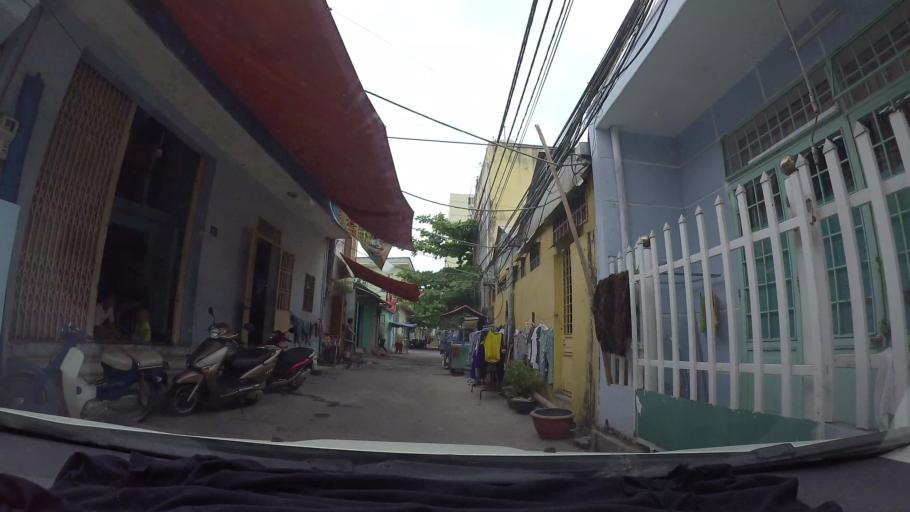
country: VN
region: Da Nang
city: Thanh Khe
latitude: 16.0731
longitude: 108.1867
